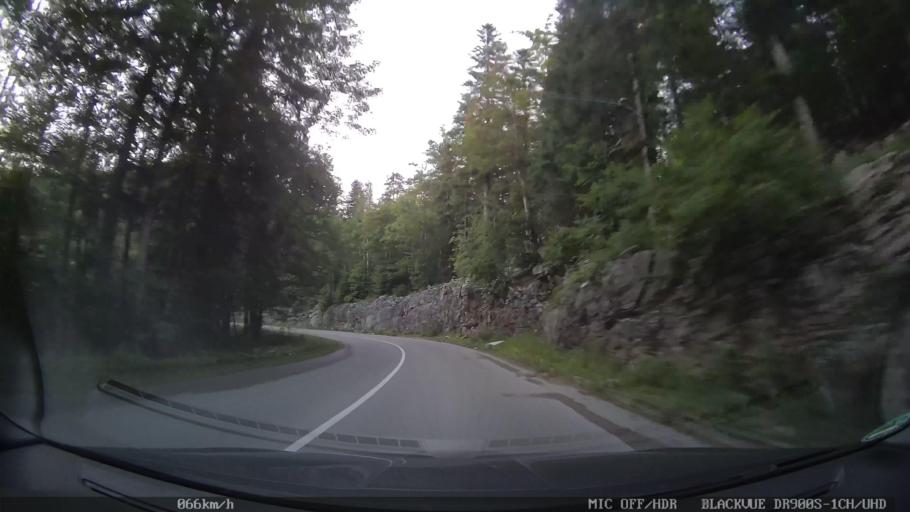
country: HR
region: Primorsko-Goranska
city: Novi Vinodolski
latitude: 45.1769
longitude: 14.9828
